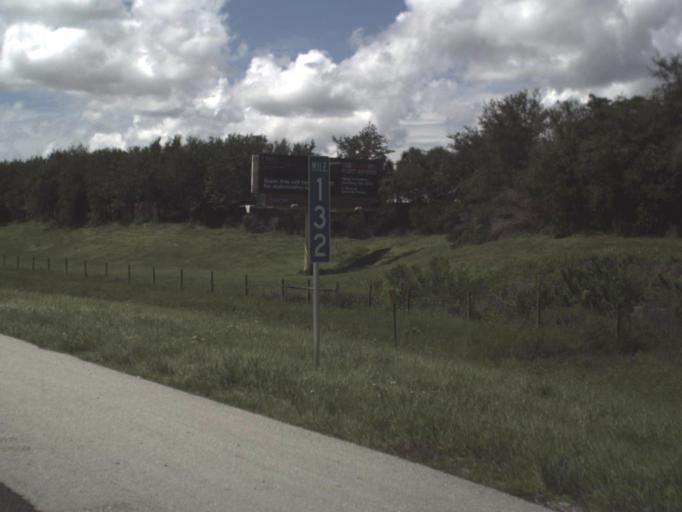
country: US
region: Florida
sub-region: Lee County
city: Gateway
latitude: 26.5550
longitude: -81.7953
